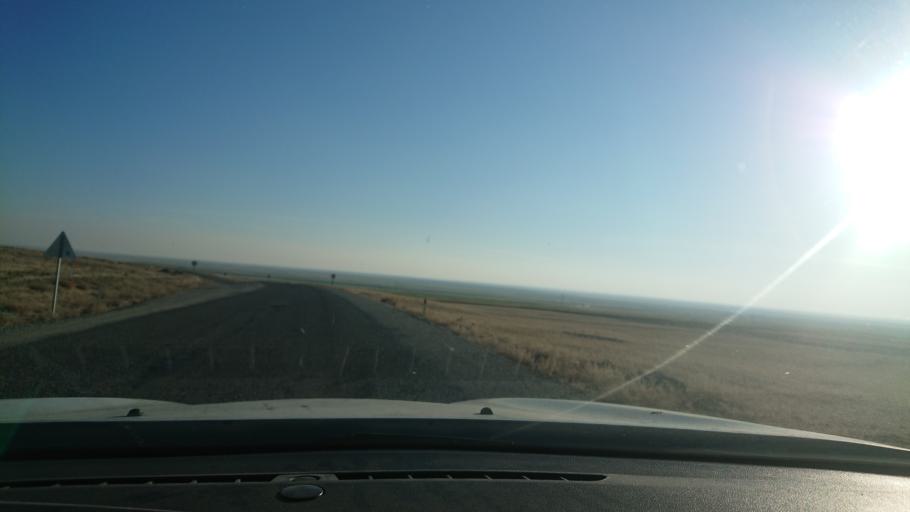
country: TR
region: Aksaray
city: Acipinar
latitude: 38.6828
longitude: 33.7347
